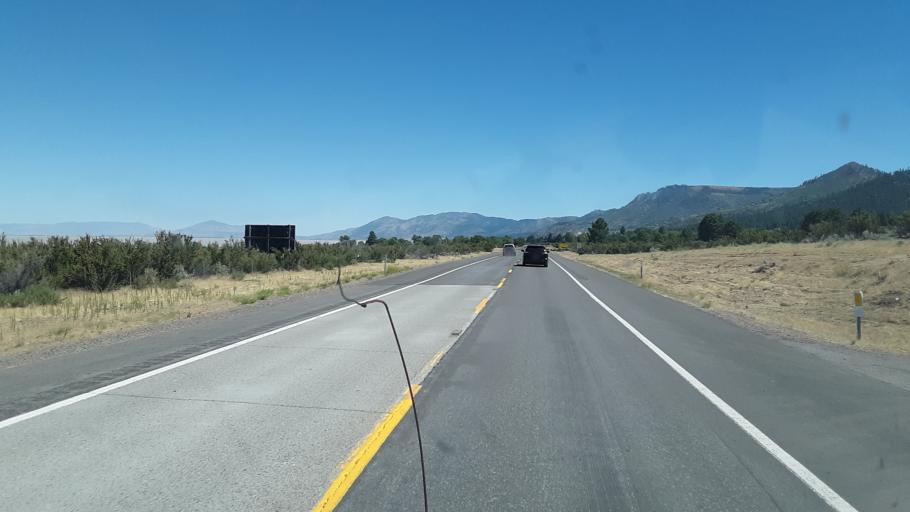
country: US
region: California
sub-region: Lassen County
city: Janesville
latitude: 40.2810
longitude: -120.4879
